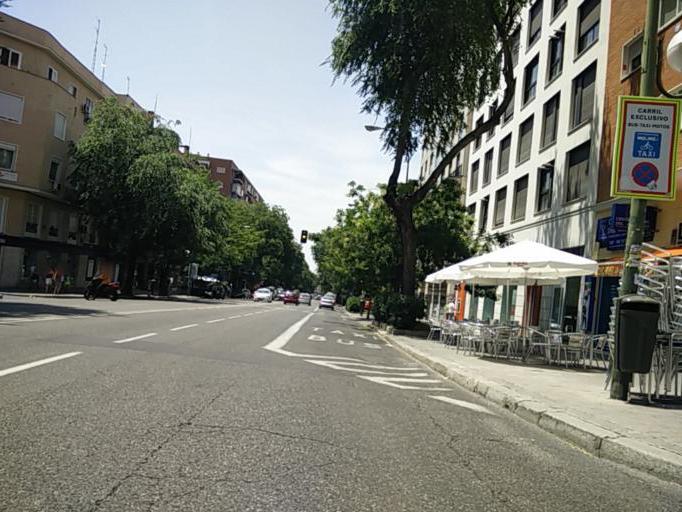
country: ES
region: Madrid
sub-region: Provincia de Madrid
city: Arganzuela
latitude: 40.4045
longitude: -3.7045
